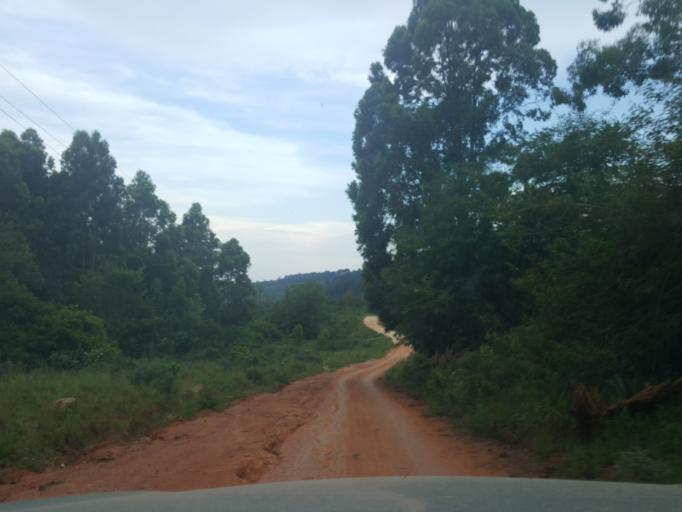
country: ZA
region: Limpopo
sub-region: Mopani District Municipality
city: Hoedspruit
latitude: -24.5925
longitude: 30.8830
